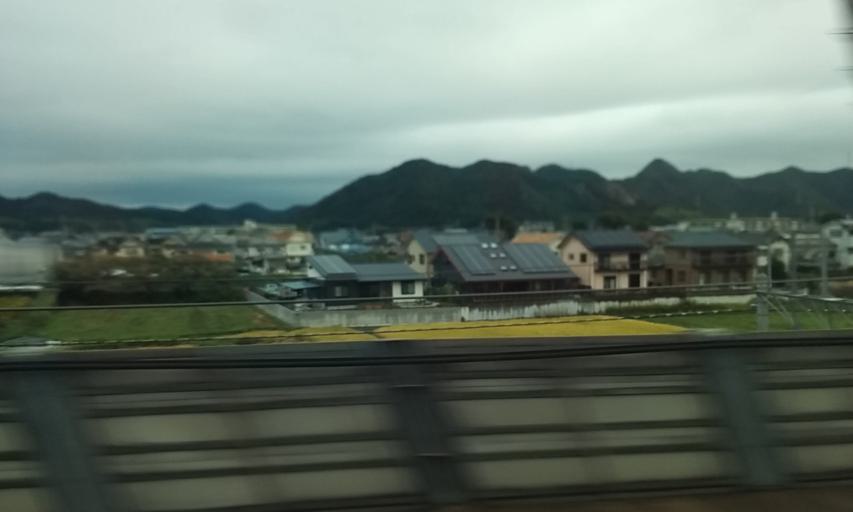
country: JP
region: Hyogo
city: Himeji
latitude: 34.8151
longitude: 134.7380
